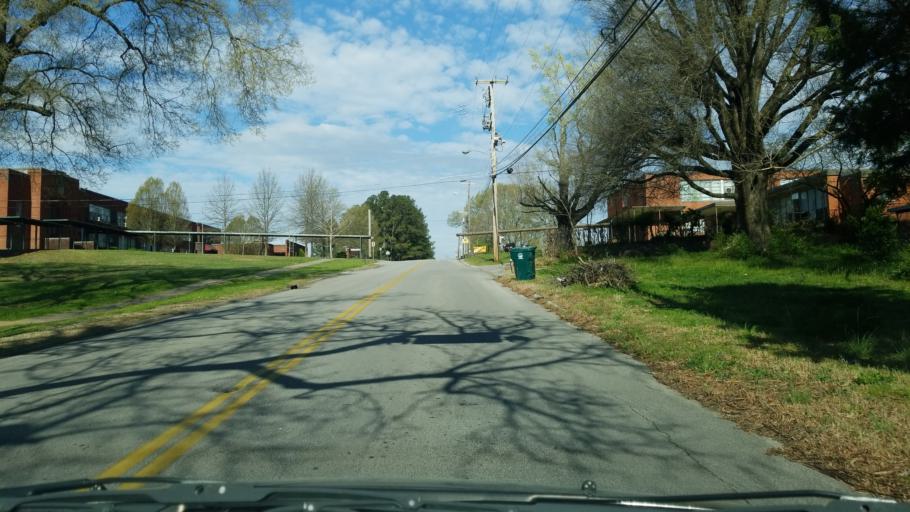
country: US
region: Tennessee
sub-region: Hamilton County
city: Harrison
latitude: 35.0612
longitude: -85.1527
